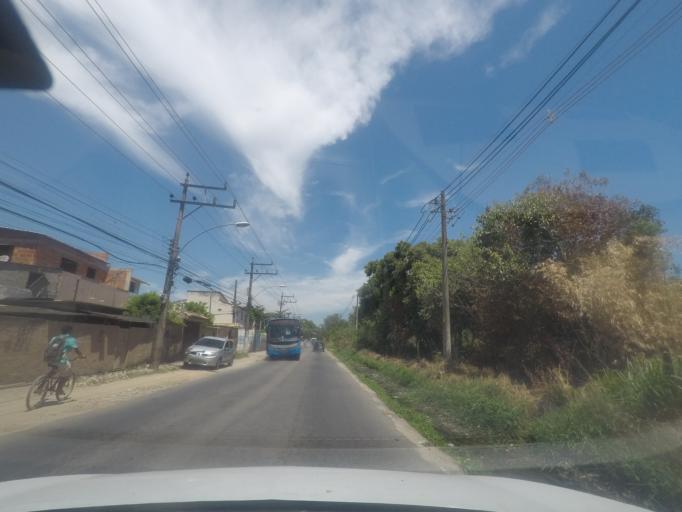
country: BR
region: Rio de Janeiro
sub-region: Itaguai
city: Itaguai
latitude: -22.9870
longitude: -43.6539
